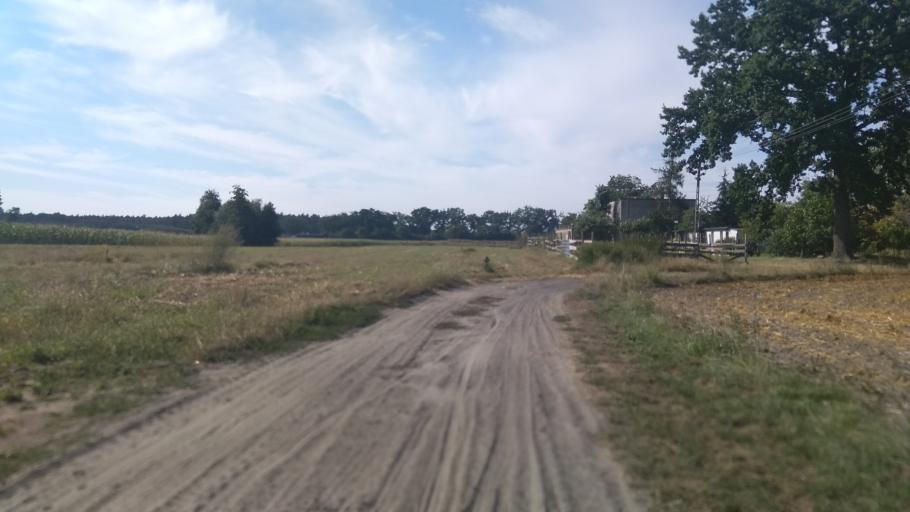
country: PL
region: Kujawsko-Pomorskie
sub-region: Powiat bydgoski
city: Osielsko
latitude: 53.2222
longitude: 18.1365
